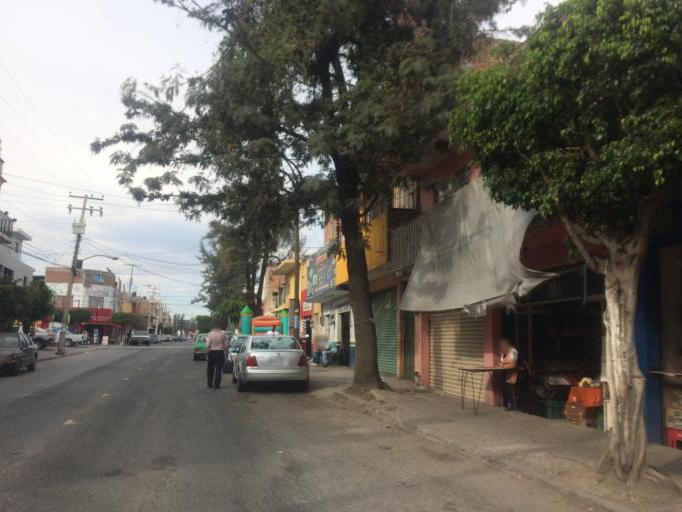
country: MX
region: Guanajuato
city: Leon
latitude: 21.1364
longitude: -101.6938
